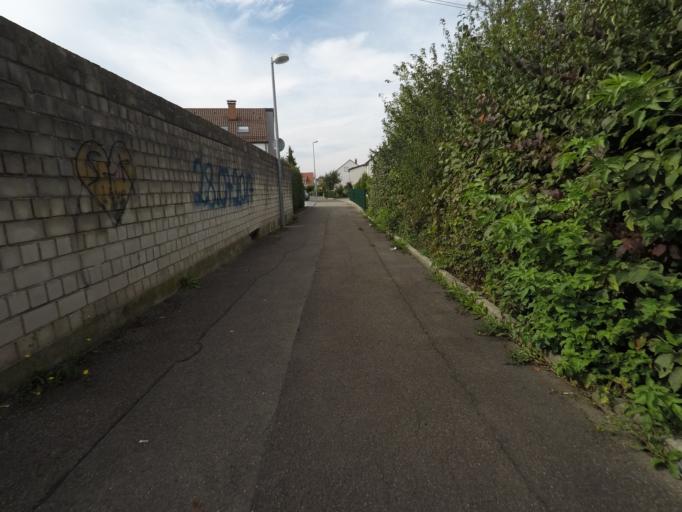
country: DE
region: Baden-Wuerttemberg
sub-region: Regierungsbezirk Stuttgart
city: Ehningen
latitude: 48.6647
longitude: 8.9523
